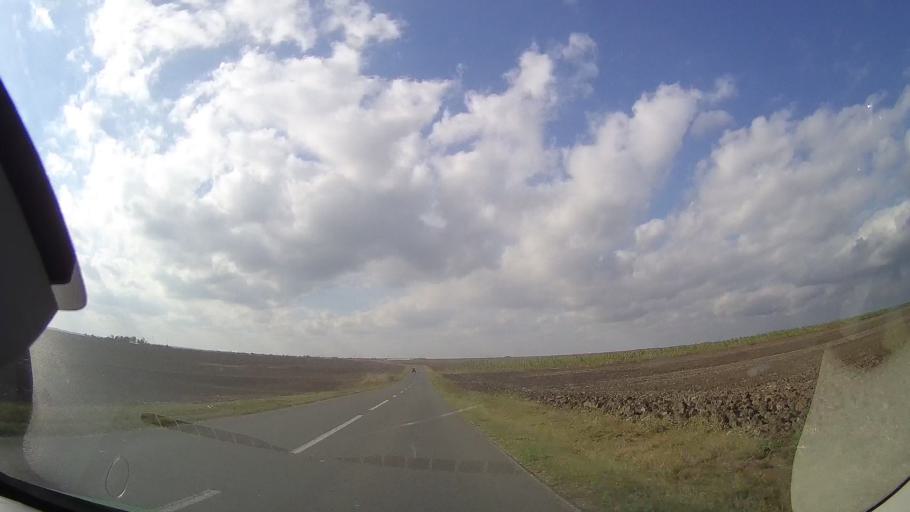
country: RO
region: Constanta
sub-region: Comuna Douazeci si Trei August
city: Douazeci si Trei August
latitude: 43.9138
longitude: 28.5648
